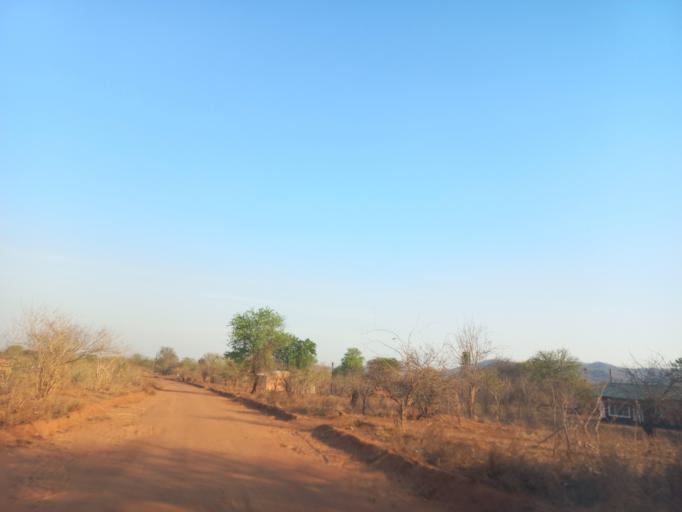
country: ZM
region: Lusaka
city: Luangwa
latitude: -15.4446
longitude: 30.3646
